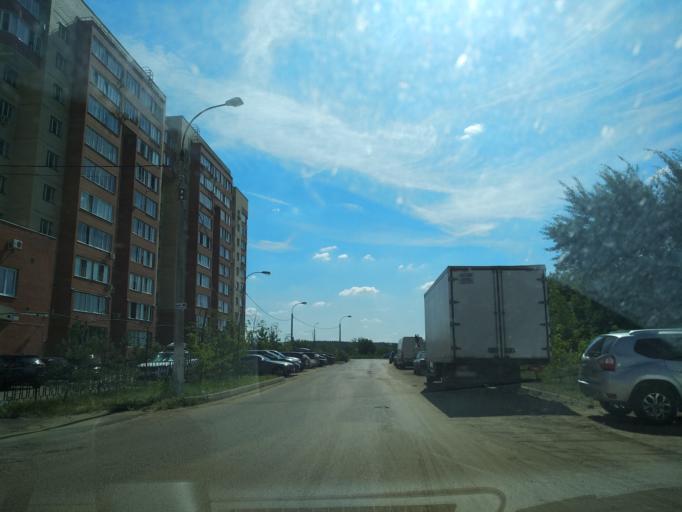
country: RU
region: Moskovskaya
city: Bykovo
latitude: 55.5927
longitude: 38.0891
